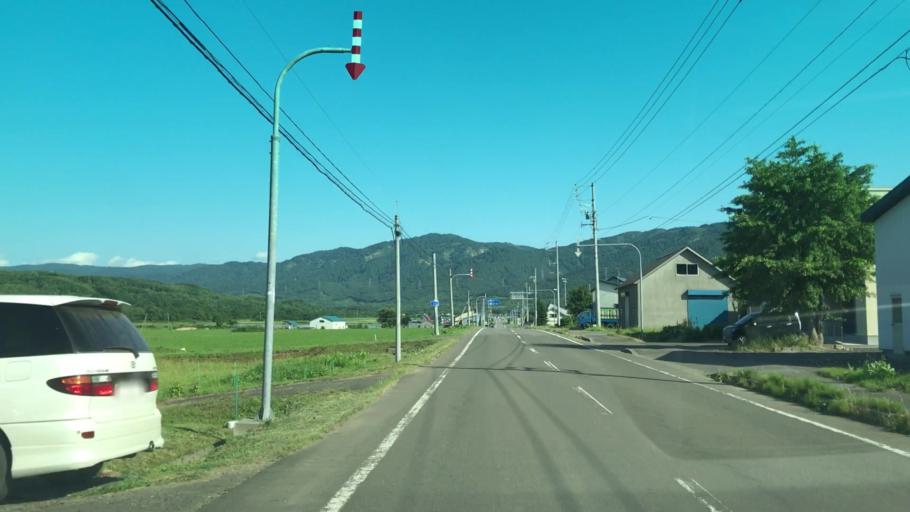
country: JP
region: Hokkaido
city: Yoichi
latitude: 43.0561
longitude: 140.7168
